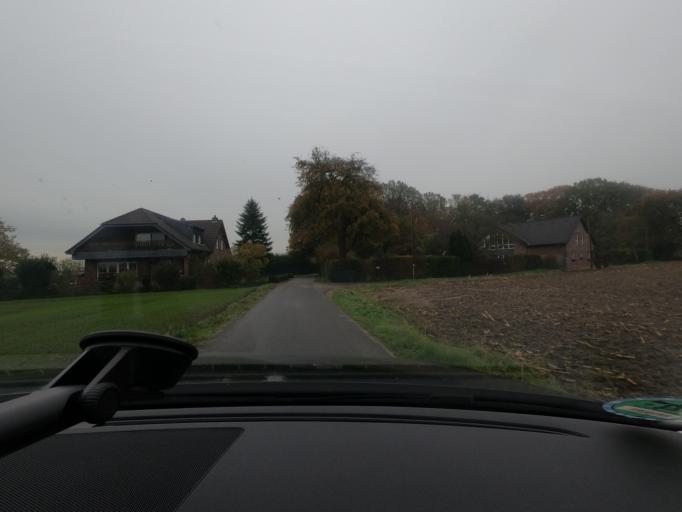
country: DE
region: North Rhine-Westphalia
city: Kempen
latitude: 51.3804
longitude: 6.3828
